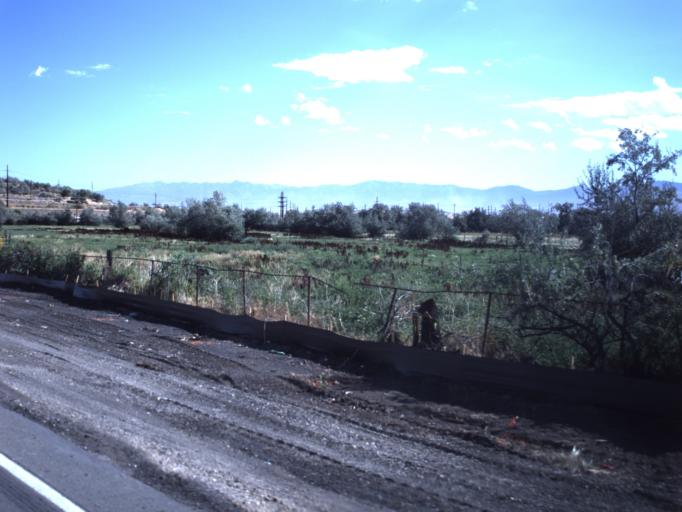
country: US
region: Utah
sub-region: Salt Lake County
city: Magna
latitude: 40.7132
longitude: -112.0916
